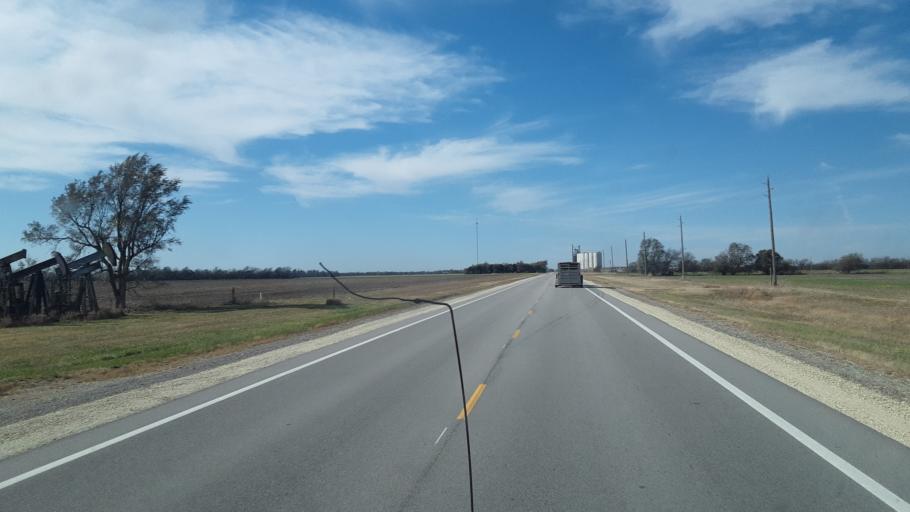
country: US
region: Kansas
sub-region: McPherson County
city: Moundridge
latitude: 38.3769
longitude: -97.4476
